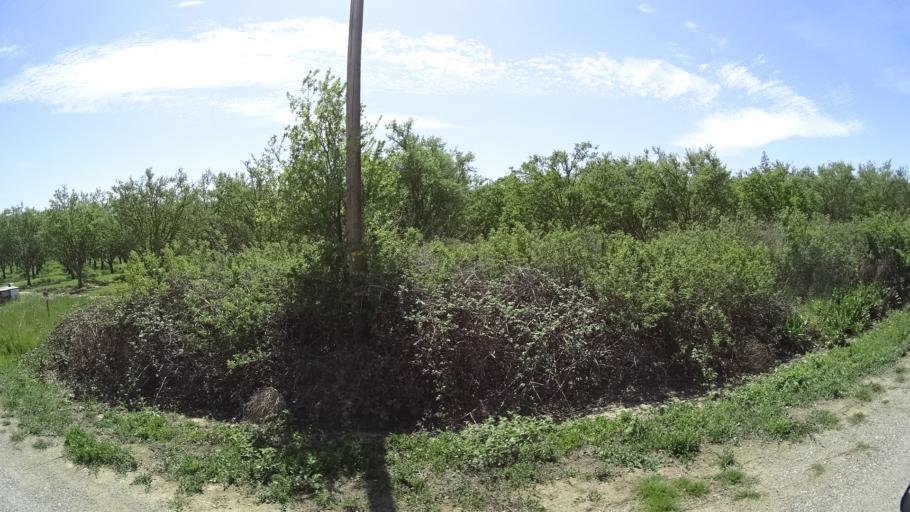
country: US
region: California
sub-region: Glenn County
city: Orland
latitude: 39.6389
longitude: -122.1999
